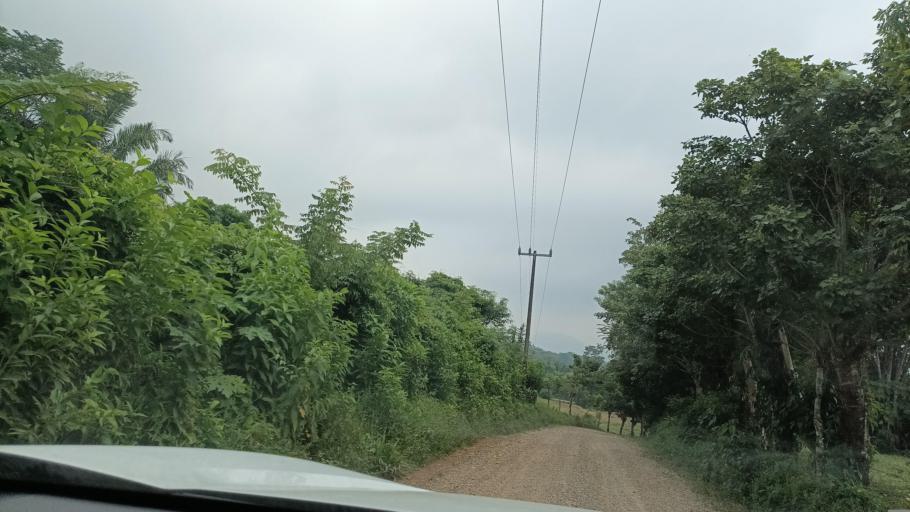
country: MX
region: Veracruz
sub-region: Uxpanapa
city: Poblado 10
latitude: 17.5482
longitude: -94.2279
